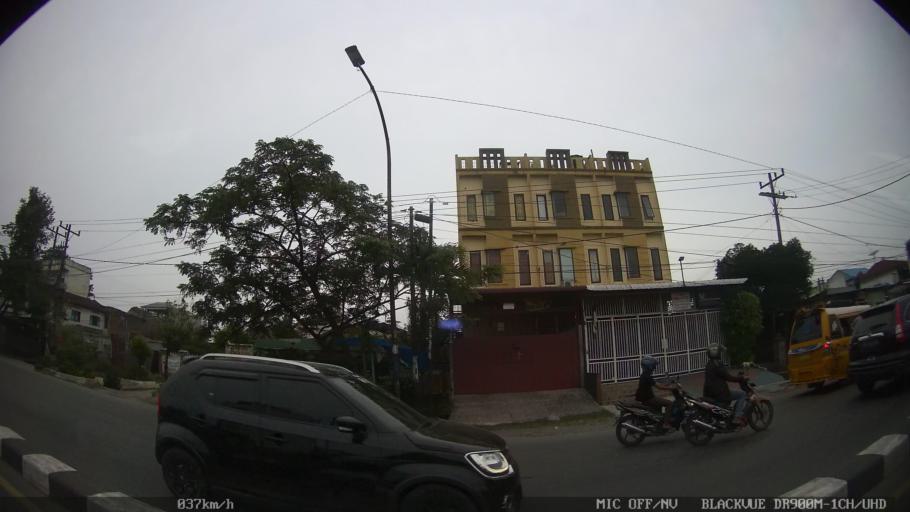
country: ID
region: North Sumatra
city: Medan
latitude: 3.5973
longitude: 98.7199
